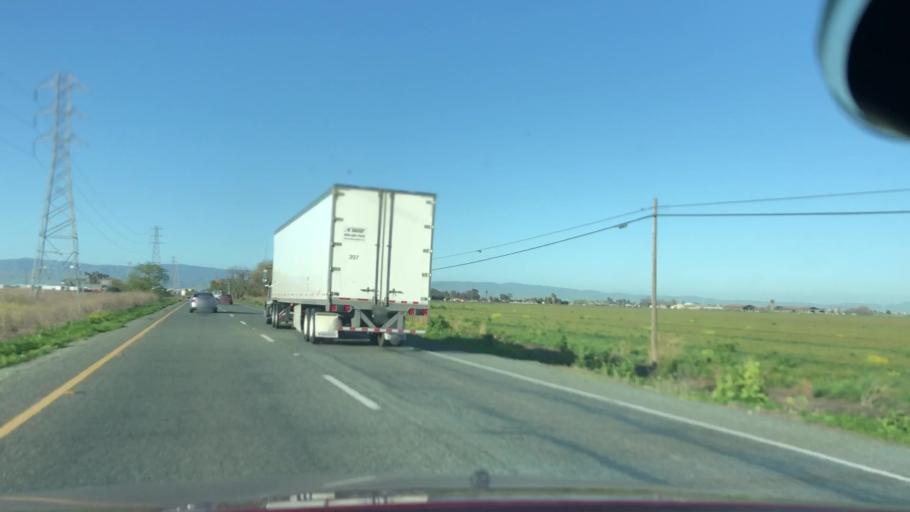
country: US
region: California
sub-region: San Joaquin County
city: Tracy
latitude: 37.7582
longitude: -121.3450
